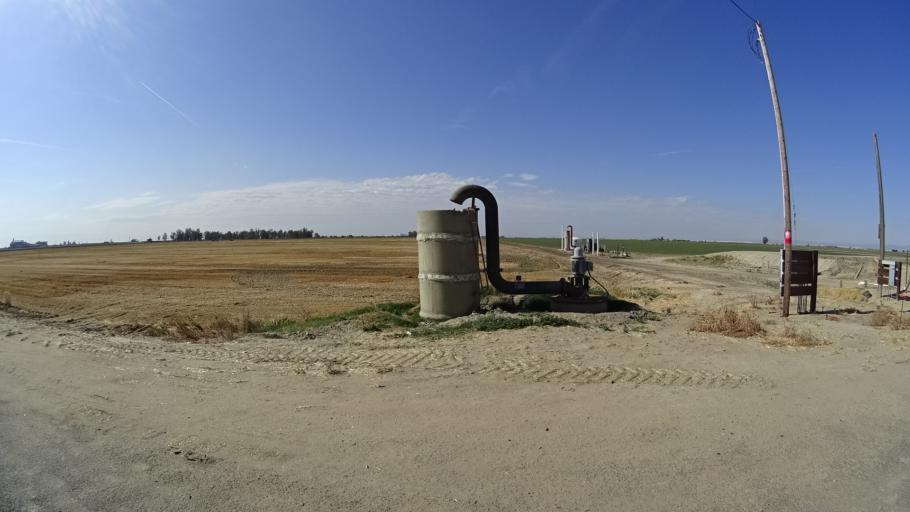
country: US
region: California
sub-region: Kings County
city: Home Garden
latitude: 36.2257
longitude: -119.6638
